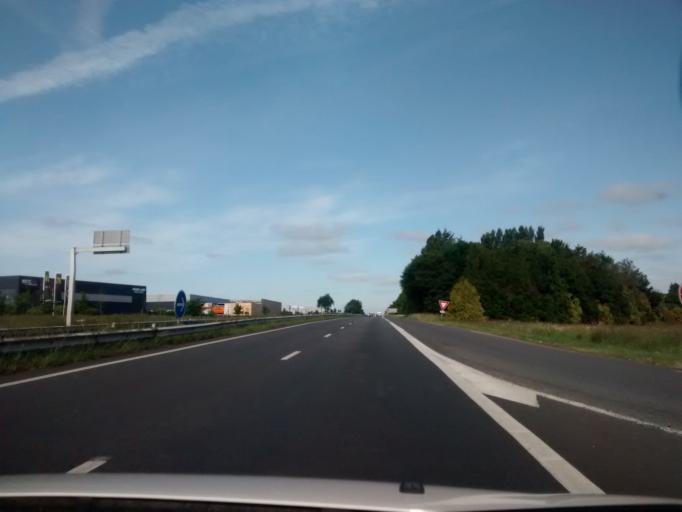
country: FR
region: Brittany
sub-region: Departement des Cotes-d'Armor
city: Lamballe
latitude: 48.4551
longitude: -2.4970
